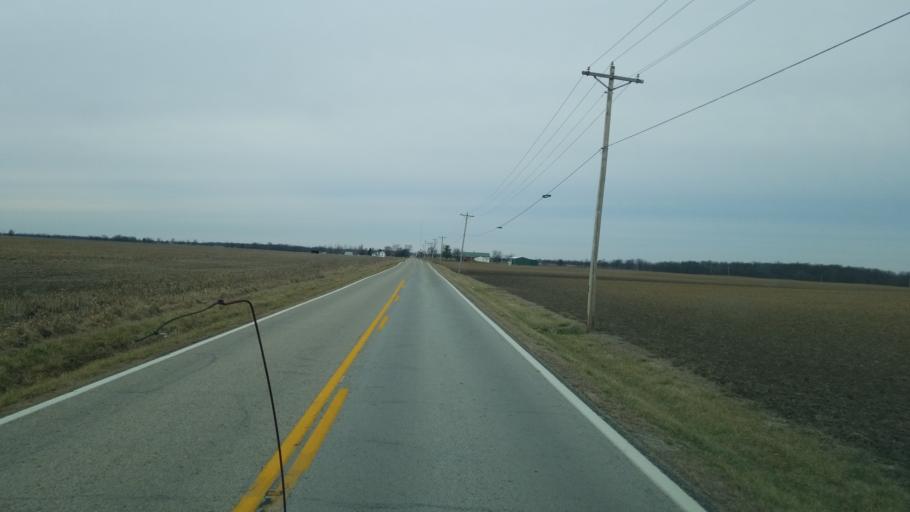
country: US
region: Ohio
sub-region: Pickaway County
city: Williamsport
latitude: 39.5286
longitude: -83.1251
